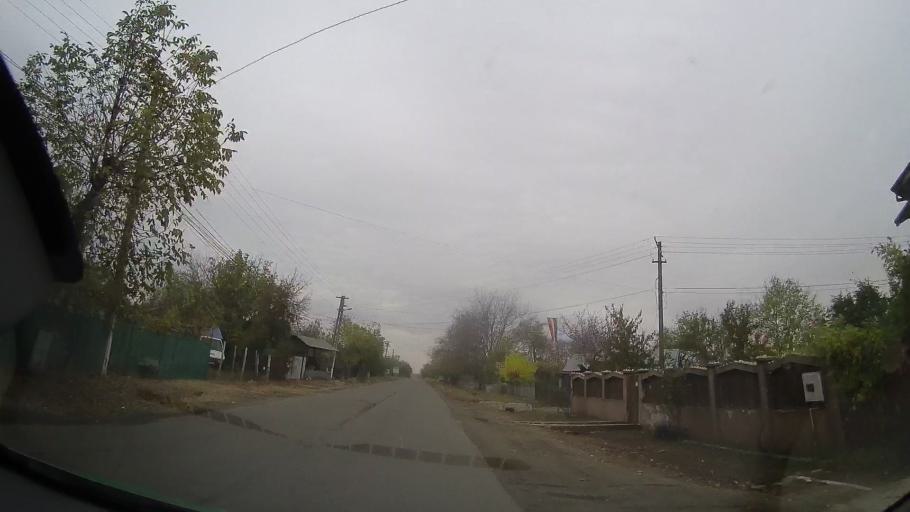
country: RO
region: Prahova
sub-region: Comuna Ceptura
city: Ceptura de Jos
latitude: 45.0158
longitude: 26.3396
